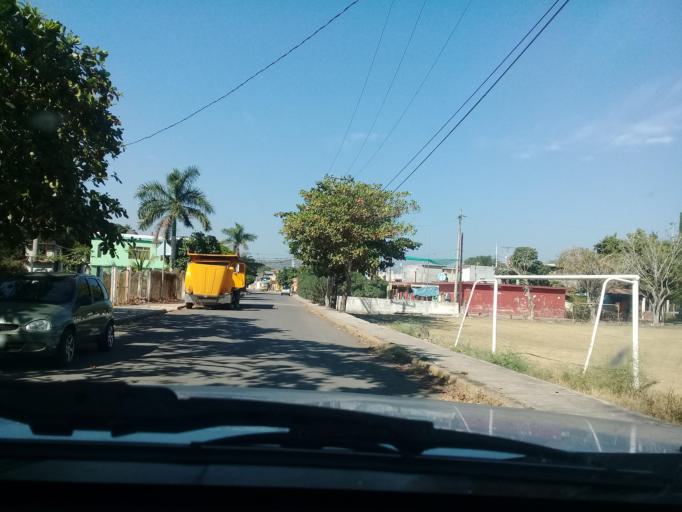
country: MX
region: Veracruz
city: Actopan
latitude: 19.4780
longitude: -96.5585
